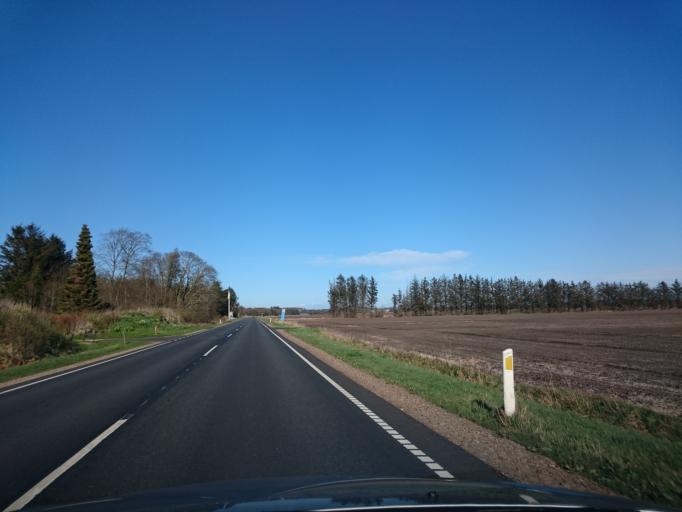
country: DK
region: North Denmark
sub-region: Hjorring Kommune
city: Sindal
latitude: 57.6014
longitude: 10.3189
